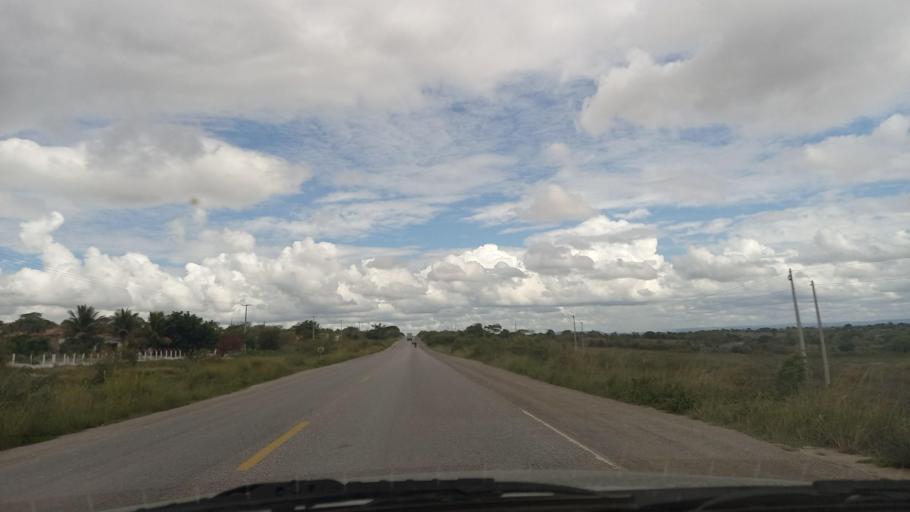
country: BR
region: Pernambuco
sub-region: Cachoeirinha
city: Cachoeirinha
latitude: -8.3657
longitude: -36.1723
